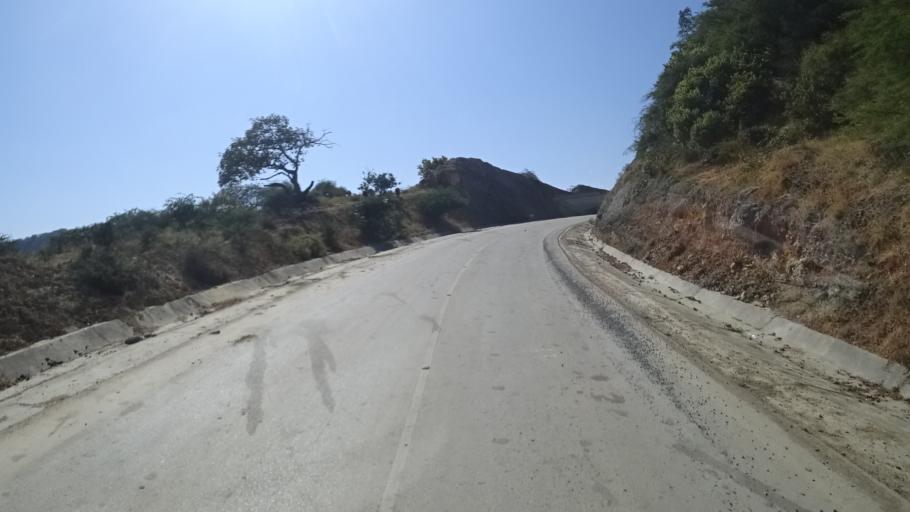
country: OM
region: Zufar
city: Salalah
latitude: 17.0611
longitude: 54.6072
